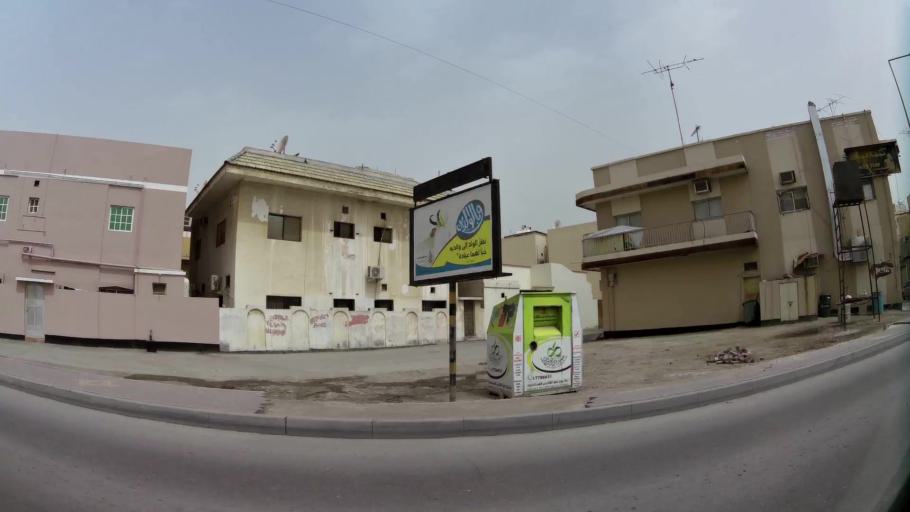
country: BH
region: Northern
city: Madinat `Isa
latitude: 26.1796
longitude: 50.5497
